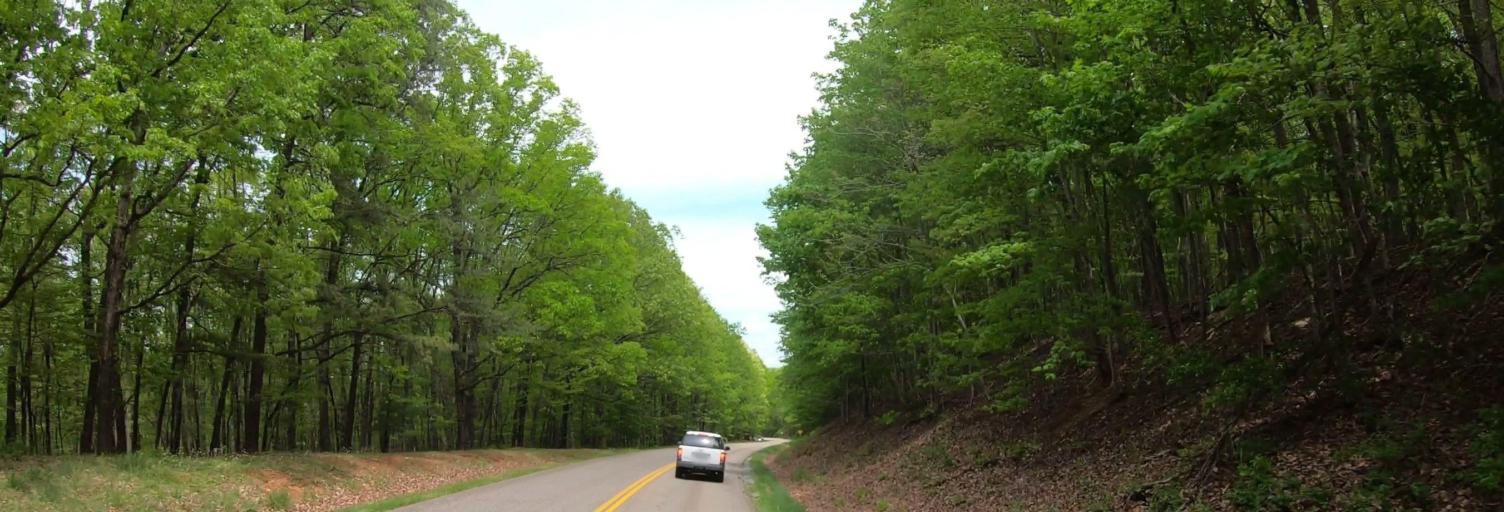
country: US
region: Virginia
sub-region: Roanoke County
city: Narrows
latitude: 37.2230
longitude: -79.9421
